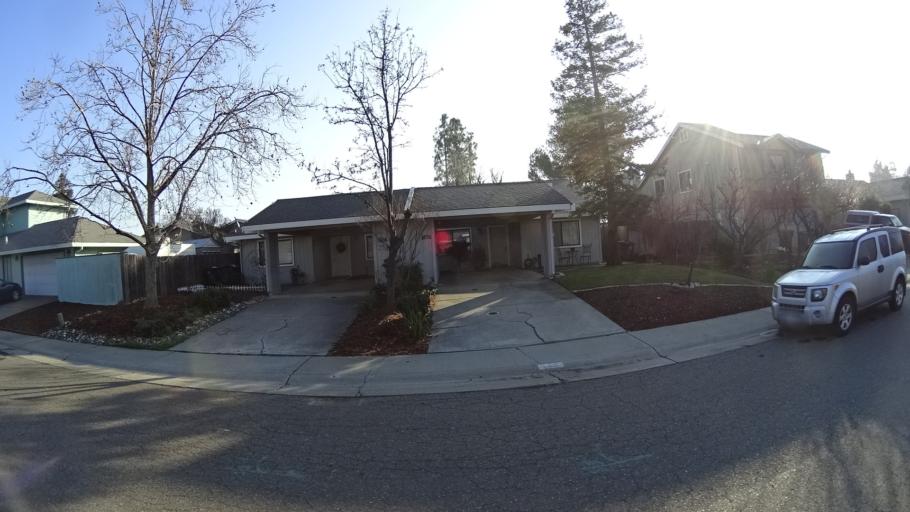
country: US
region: California
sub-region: Yolo County
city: Davis
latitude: 38.5599
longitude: -121.7907
